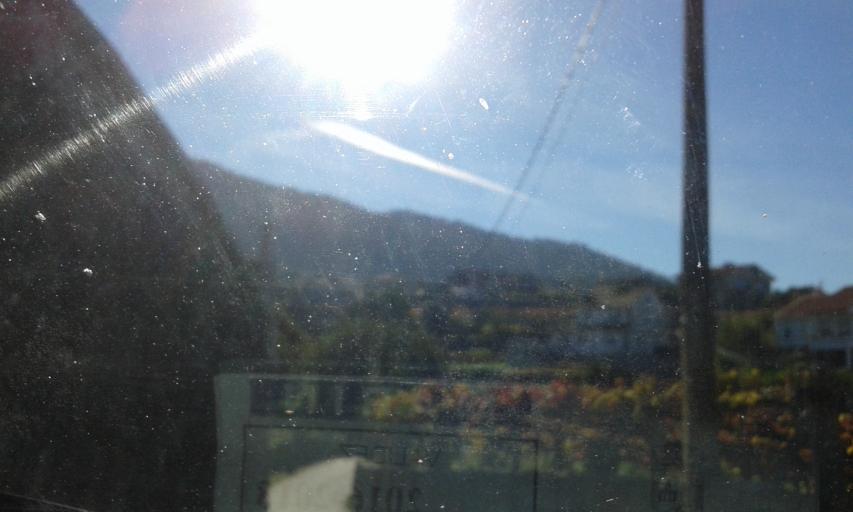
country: ES
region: Galicia
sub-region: Provincia de Pontevedra
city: Bueu
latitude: 42.3502
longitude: -8.7487
